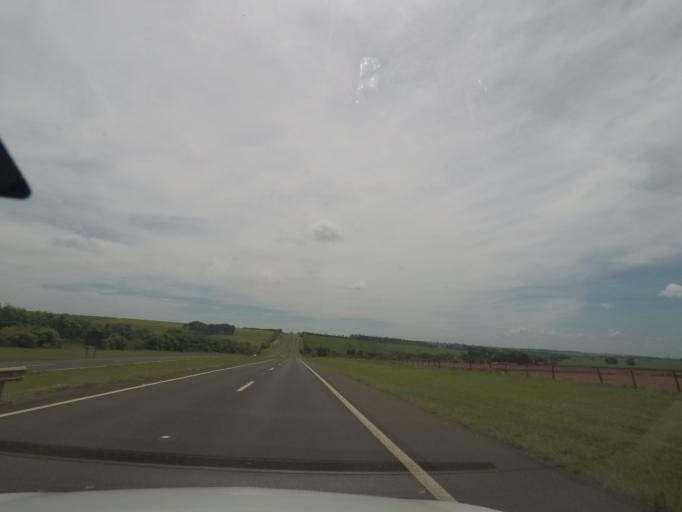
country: BR
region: Sao Paulo
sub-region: Bebedouro
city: Bebedouro
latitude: -21.0201
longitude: -48.4241
